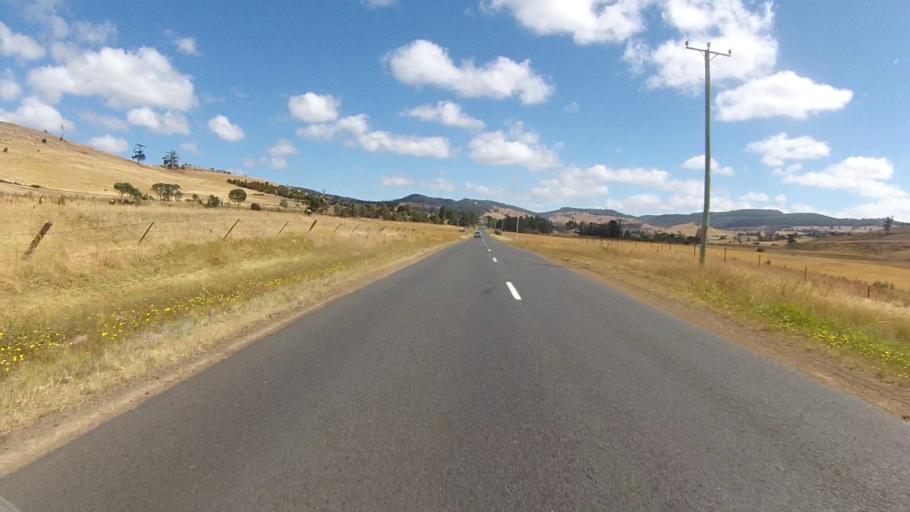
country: AU
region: Tasmania
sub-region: Brighton
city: Bridgewater
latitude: -42.5409
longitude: 147.3700
